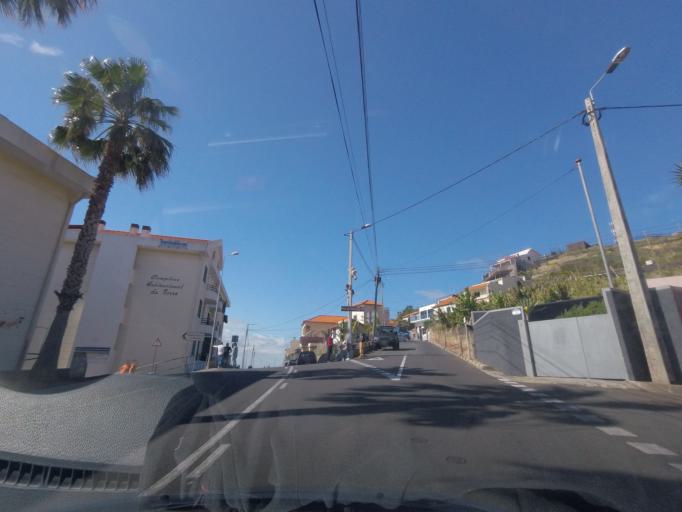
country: PT
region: Madeira
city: Camara de Lobos
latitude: 32.6532
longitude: -16.9716
